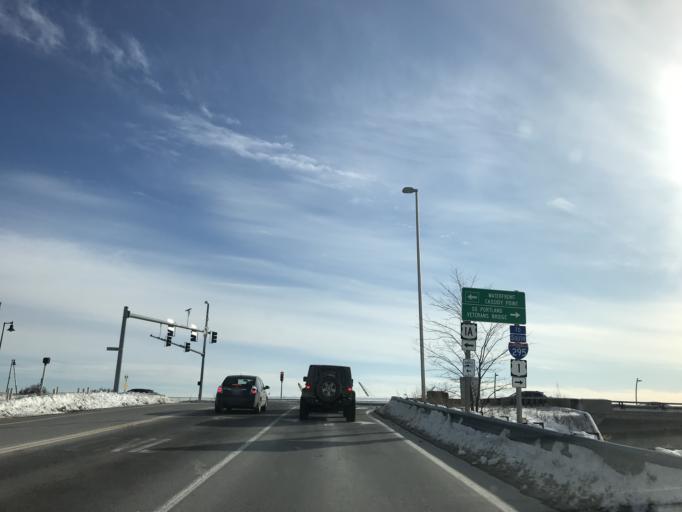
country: US
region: Maine
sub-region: Cumberland County
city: Portland
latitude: 43.6451
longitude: -70.2810
